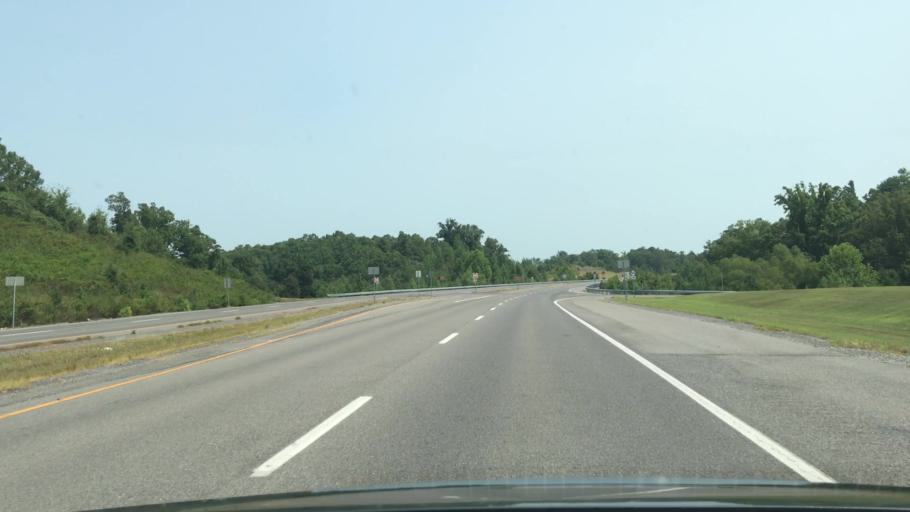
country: US
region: Kentucky
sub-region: Marshall County
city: Benton
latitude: 36.7613
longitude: -88.1487
